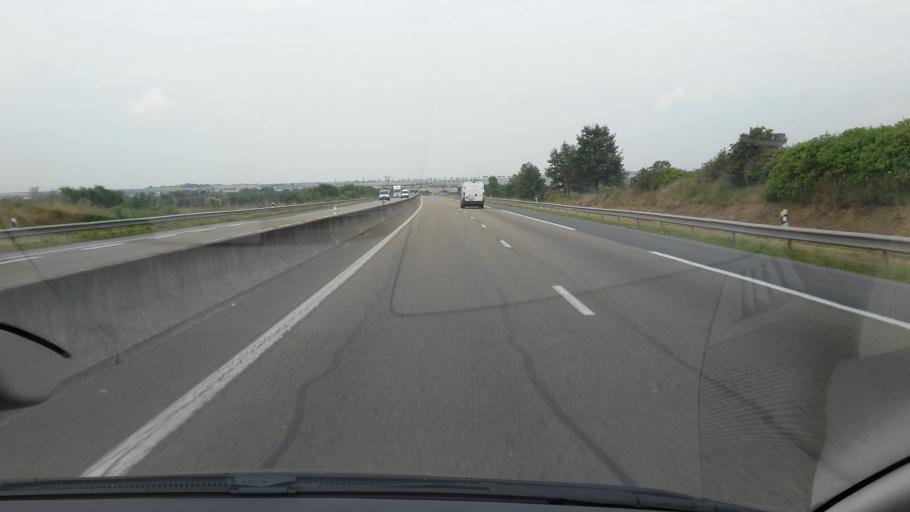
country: FR
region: Champagne-Ardenne
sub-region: Departement de la Marne
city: Cernay-les-Reims
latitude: 49.2462
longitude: 4.0817
